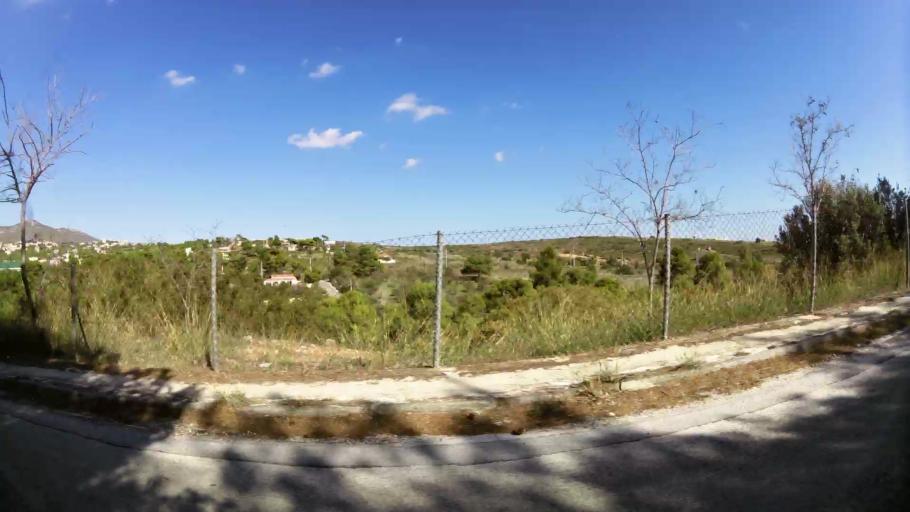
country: GR
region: Attica
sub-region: Nomarchia Anatolikis Attikis
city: Dioni
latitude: 38.0131
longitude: 23.9325
